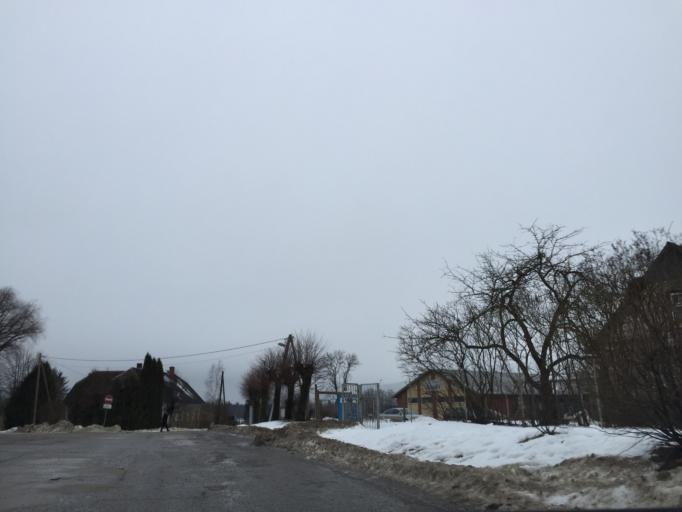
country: LV
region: Krimulda
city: Ragana
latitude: 57.1804
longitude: 24.7136
